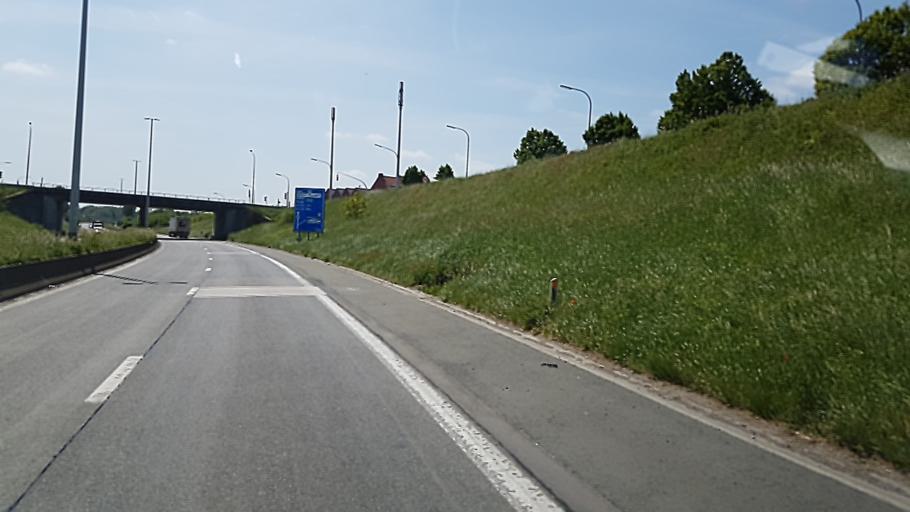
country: BE
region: Flanders
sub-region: Provincie West-Vlaanderen
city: Lendelede
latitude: 50.8452
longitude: 3.2251
